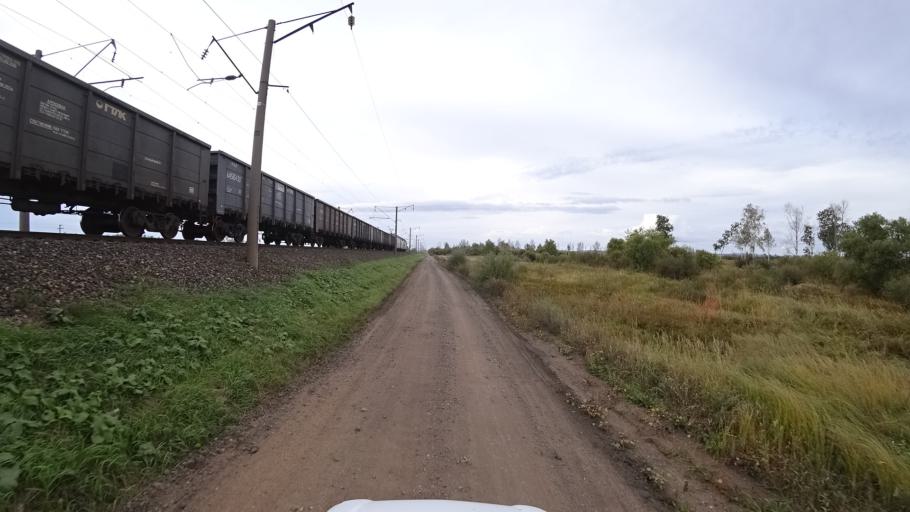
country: RU
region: Amur
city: Arkhara
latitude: 49.3585
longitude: 130.1517
